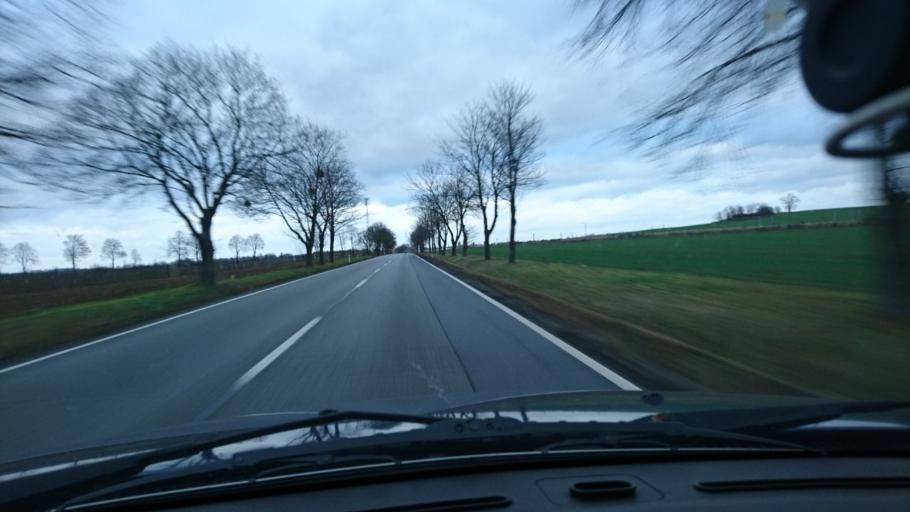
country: PL
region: Opole Voivodeship
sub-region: Powiat kluczborski
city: Byczyna
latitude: 51.0935
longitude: 18.2021
